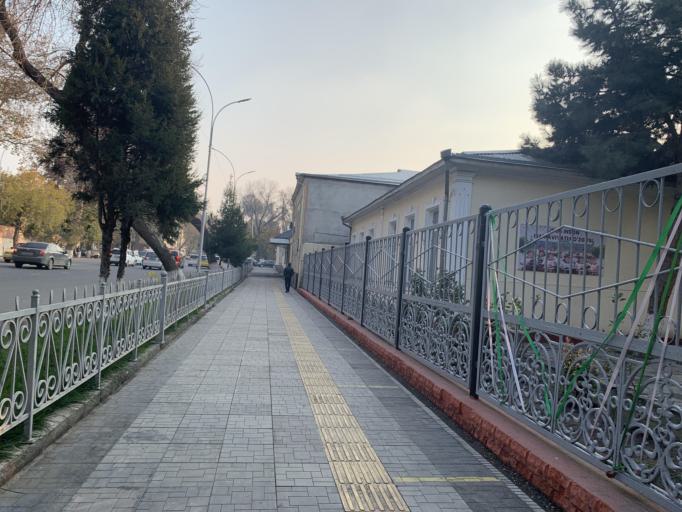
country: UZ
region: Fergana
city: Qo`qon
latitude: 40.5318
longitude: 70.9380
